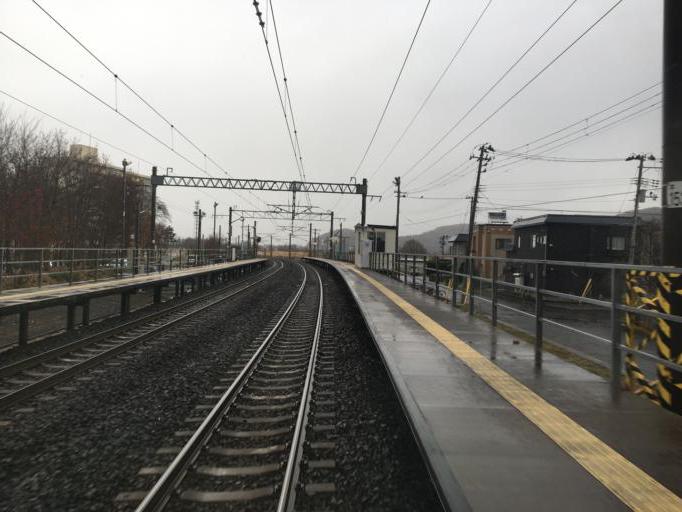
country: JP
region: Aomori
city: Aomori Shi
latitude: 40.8178
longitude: 140.7975
